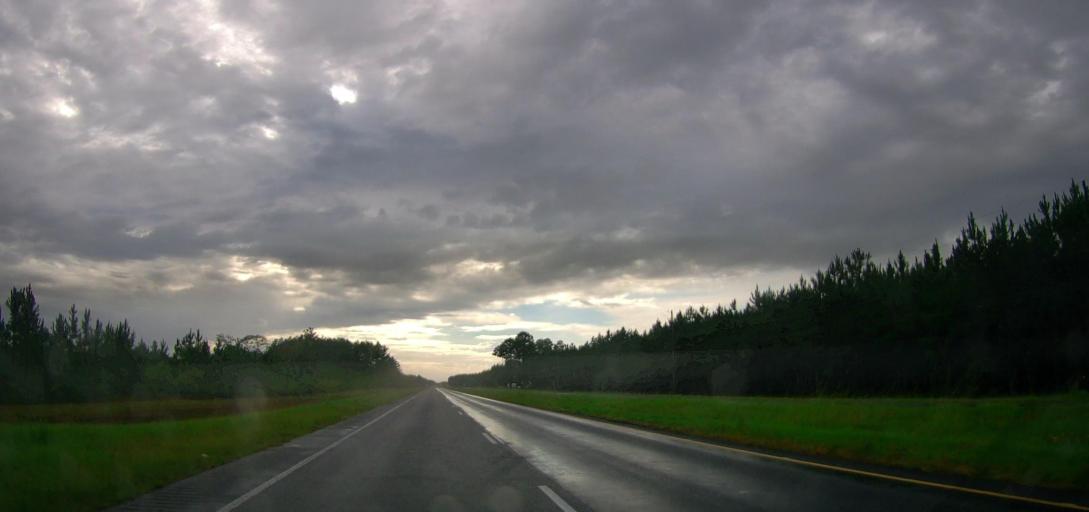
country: US
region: Georgia
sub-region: Ware County
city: Deenwood
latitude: 31.2567
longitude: -82.4926
